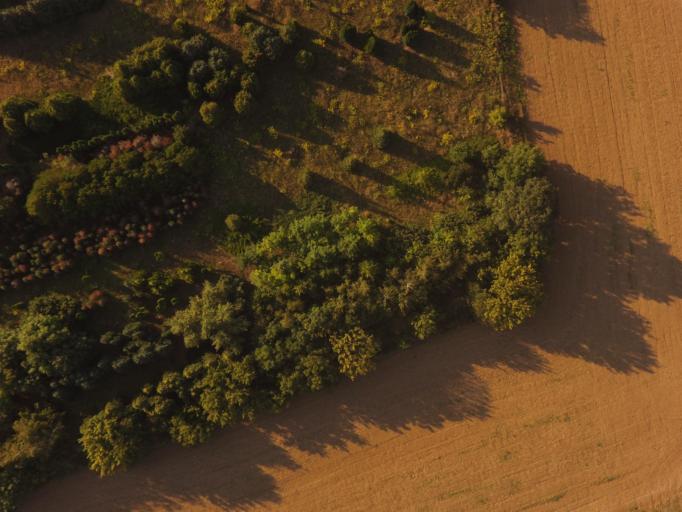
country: HU
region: Somogy
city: Balatonszarszo
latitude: 46.8123
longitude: 17.7877
